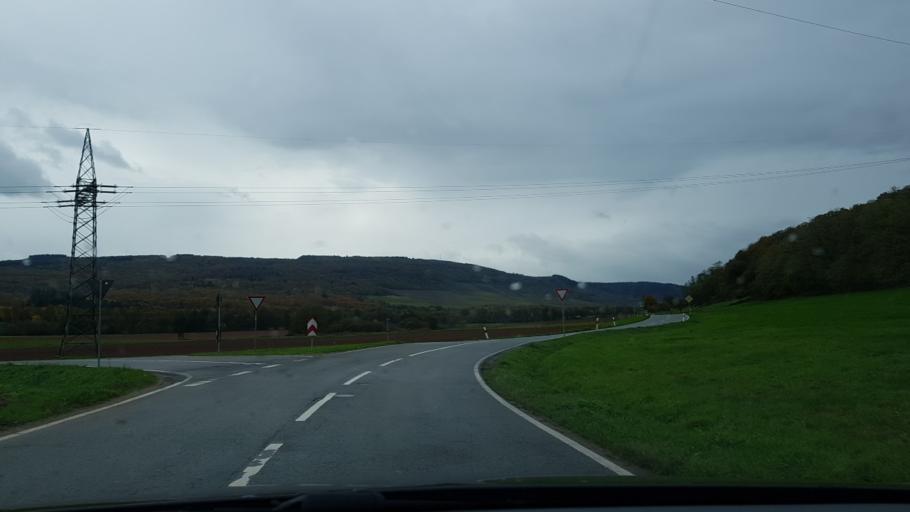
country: DE
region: Rheinland-Pfalz
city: Sehlem
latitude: 49.8968
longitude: 6.8400
